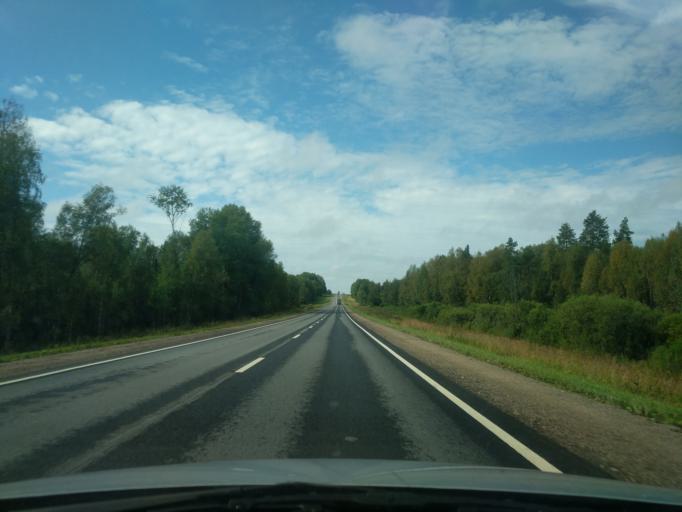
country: RU
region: Kostroma
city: Sudislavl'
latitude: 57.8381
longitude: 41.8565
